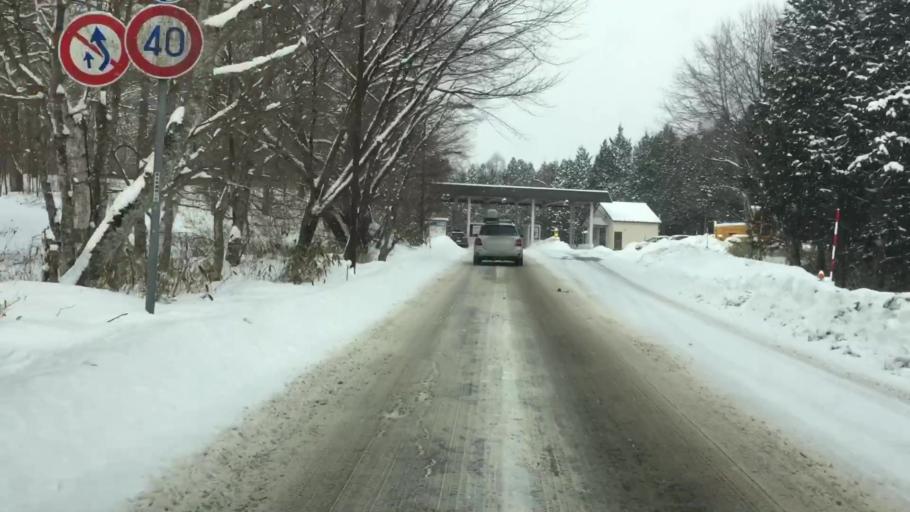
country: JP
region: Tochigi
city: Yaita
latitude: 36.9545
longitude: 139.7687
